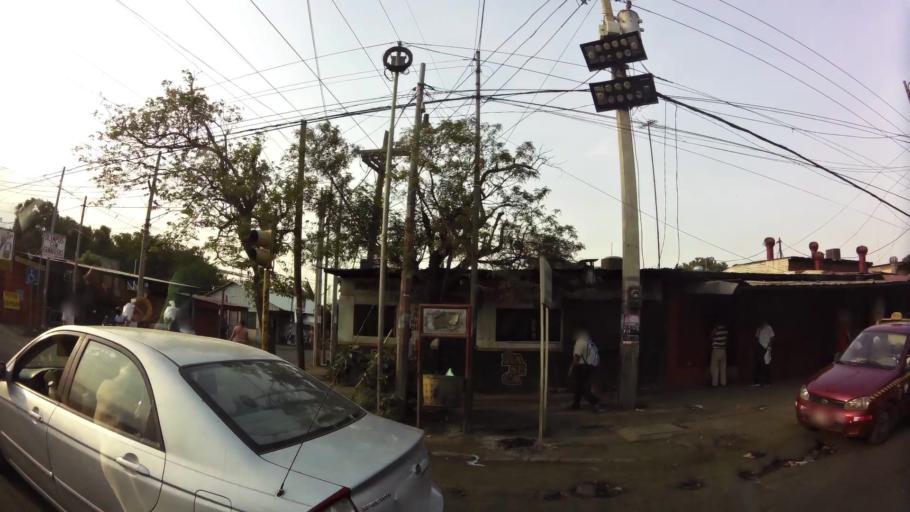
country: NI
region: Managua
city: Ciudad Sandino
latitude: 12.1229
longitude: -86.3115
